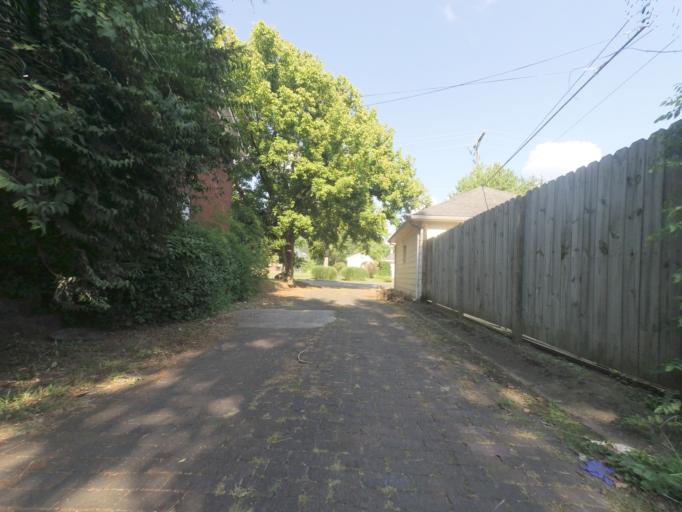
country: US
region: West Virginia
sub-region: Cabell County
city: Huntington
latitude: 38.4076
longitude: -82.4496
